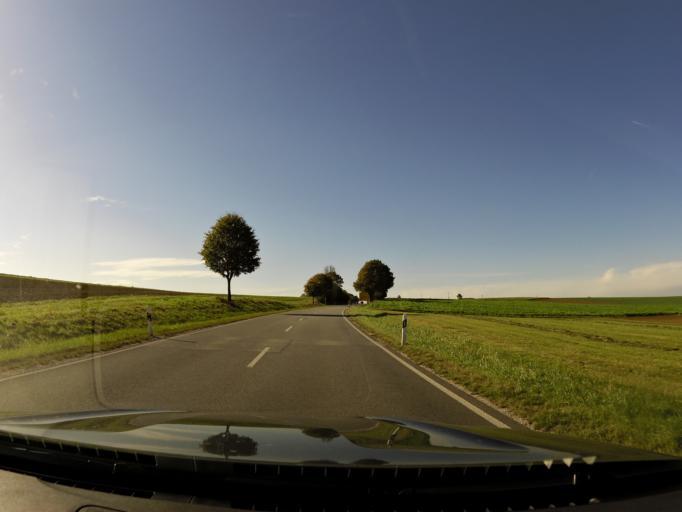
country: DE
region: Bavaria
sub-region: Lower Bavaria
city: Altfraunhofen
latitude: 48.4484
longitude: 12.1485
